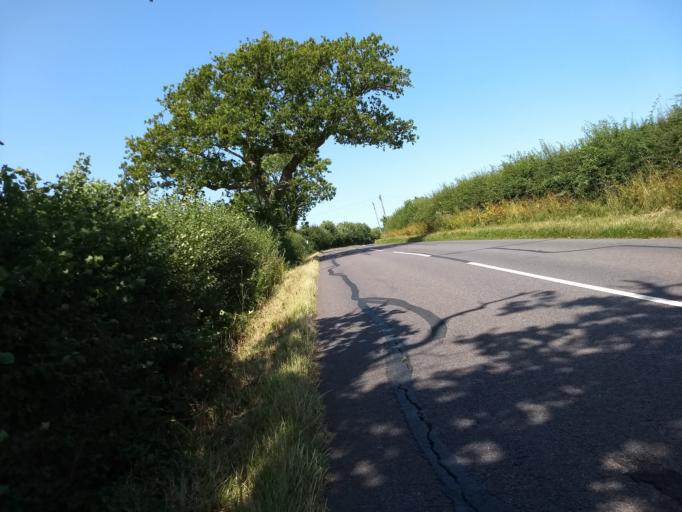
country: GB
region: England
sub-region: Isle of Wight
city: Northwood
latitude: 50.7121
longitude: -1.3507
